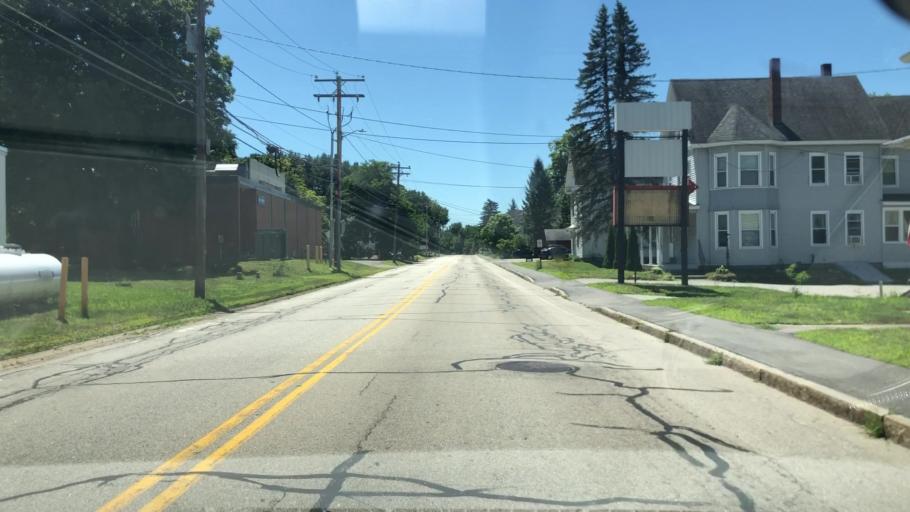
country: US
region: New Hampshire
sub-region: Hillsborough County
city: Milford
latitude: 42.8317
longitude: -71.6487
